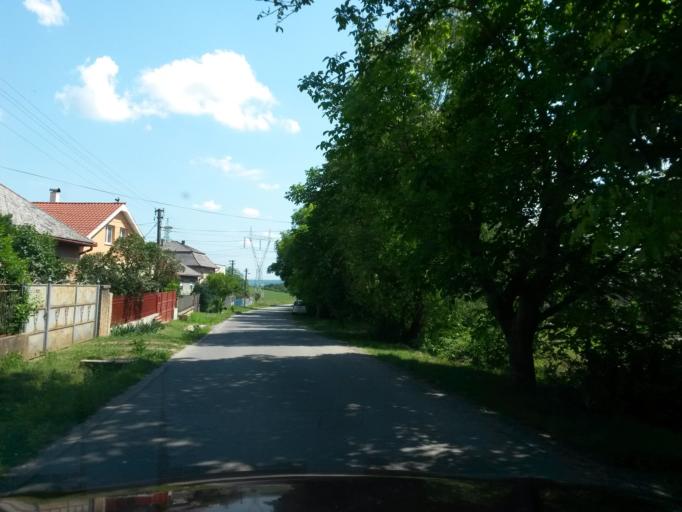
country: SK
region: Kosicky
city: Medzev
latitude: 48.6119
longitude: 20.8339
